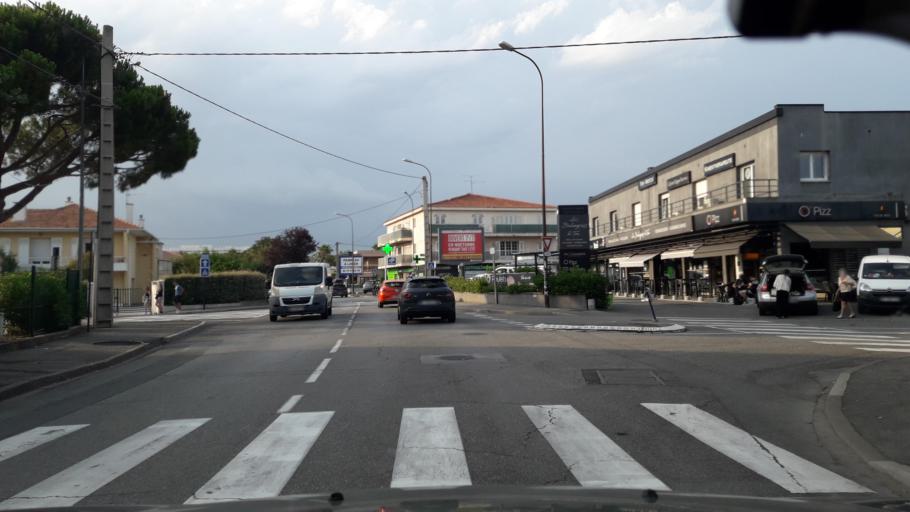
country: FR
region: Provence-Alpes-Cote d'Azur
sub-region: Departement du Var
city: Frejus
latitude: 43.4323
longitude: 6.7546
